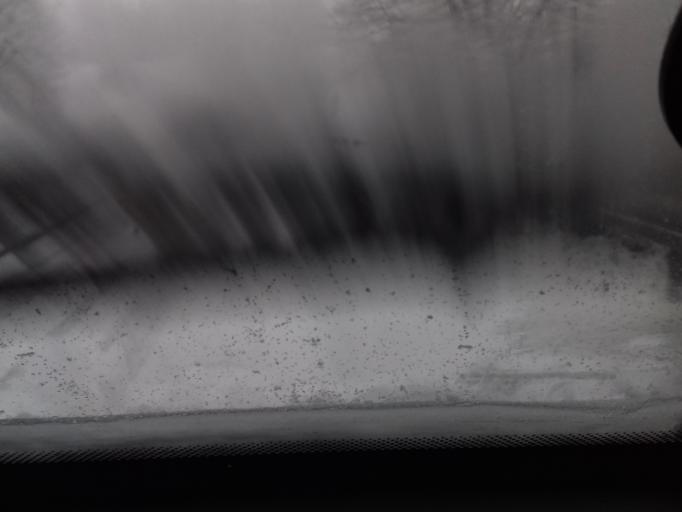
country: BA
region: Federation of Bosnia and Herzegovina
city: Lokvine
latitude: 44.2336
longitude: 17.8295
